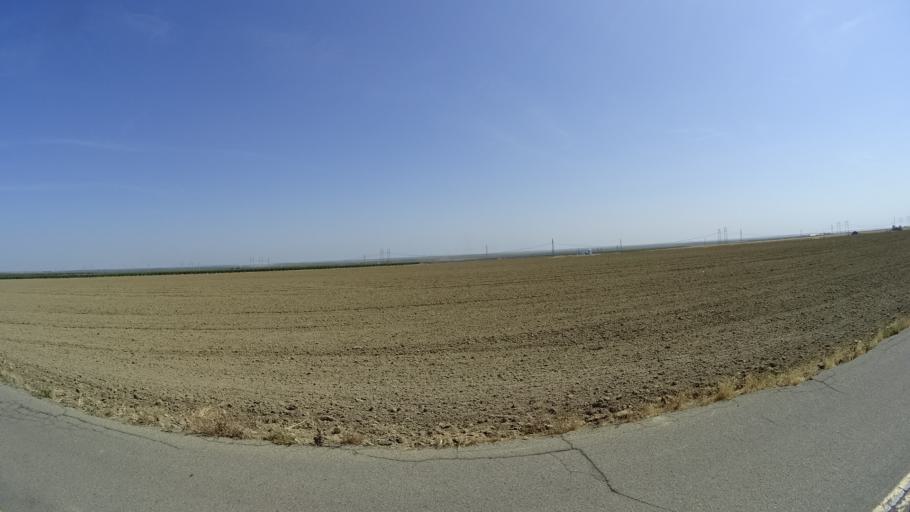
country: US
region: California
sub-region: Kings County
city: Avenal
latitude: 36.0741
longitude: -120.0811
